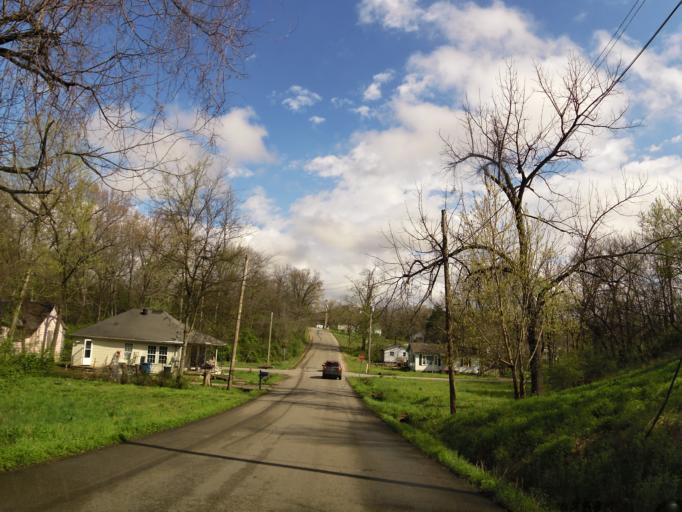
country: US
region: Missouri
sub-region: Butler County
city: Poplar Bluff
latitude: 36.7646
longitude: -90.3949
